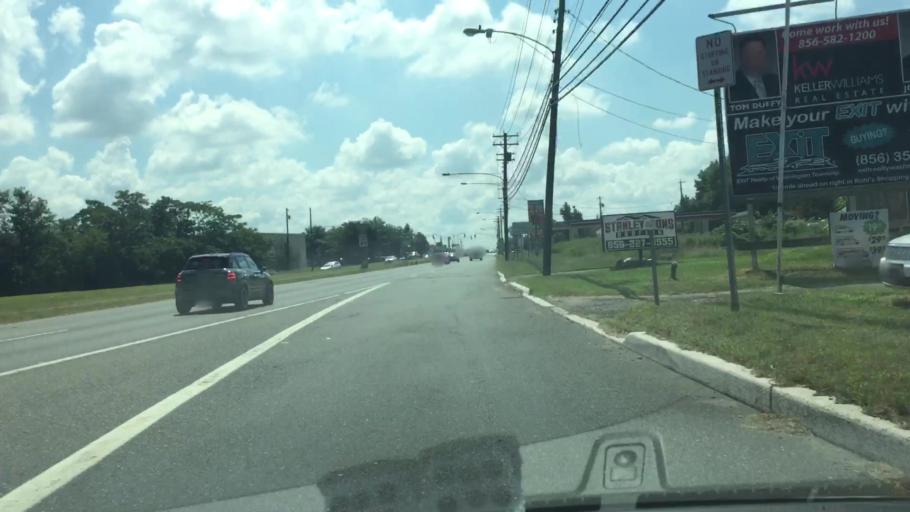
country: US
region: New Jersey
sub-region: Gloucester County
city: Turnersville
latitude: 39.7673
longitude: -75.0490
